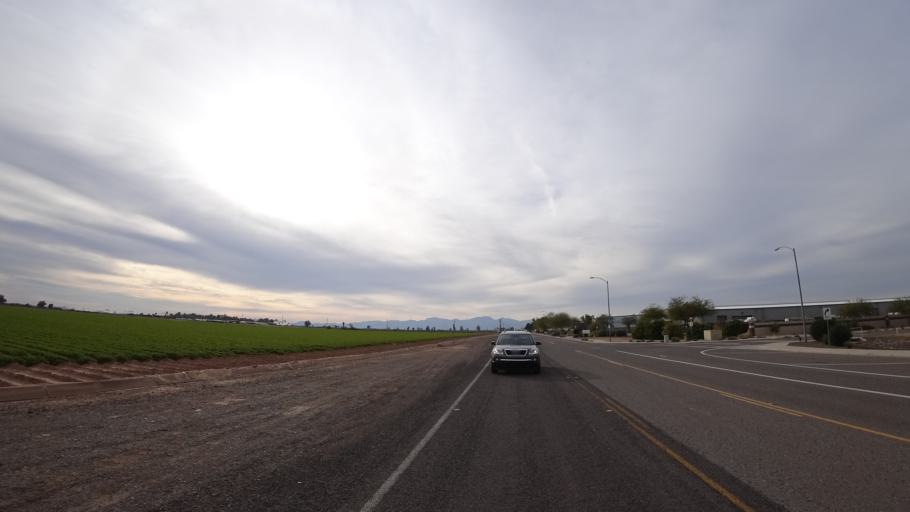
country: US
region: Arizona
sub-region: Maricopa County
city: El Mirage
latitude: 33.5801
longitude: -112.3467
